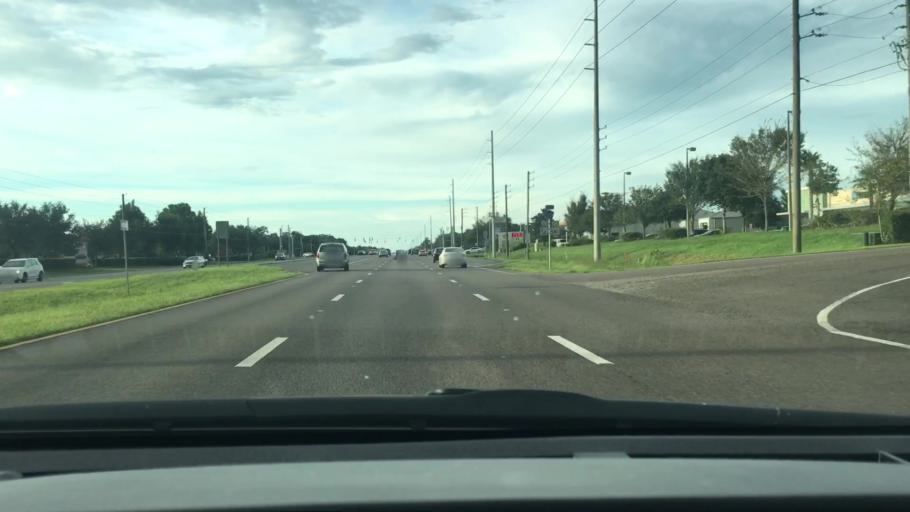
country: US
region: Florida
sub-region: Hillsborough County
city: Pebble Creek
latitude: 28.1824
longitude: -82.3535
